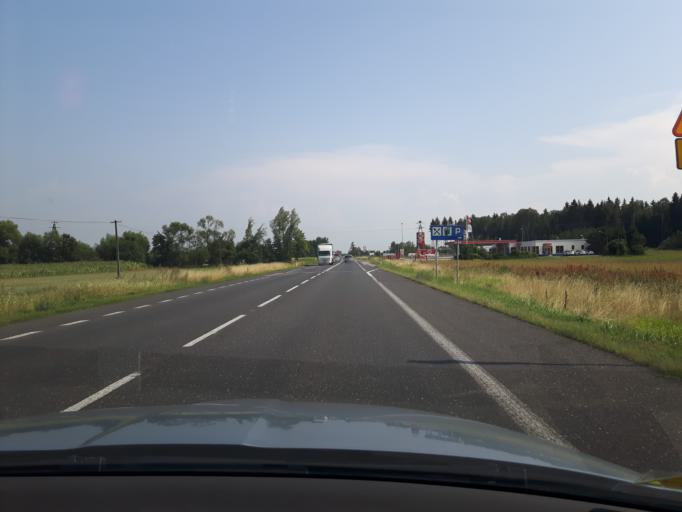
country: PL
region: Masovian Voivodeship
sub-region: Powiat plonski
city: Plonsk
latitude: 52.6994
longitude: 20.3415
